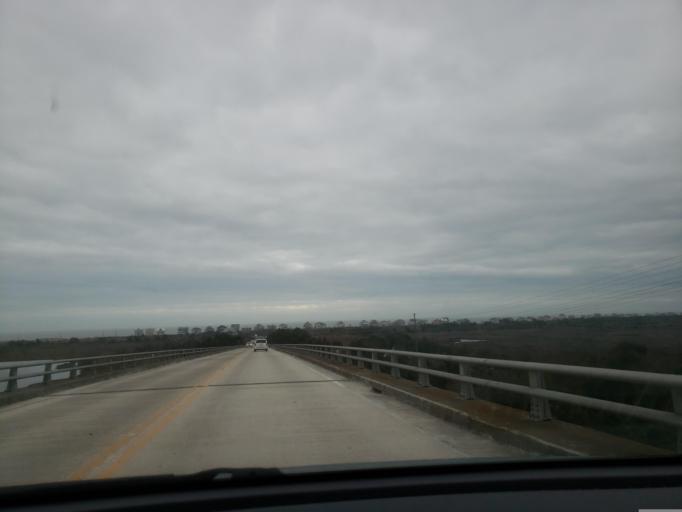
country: US
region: North Carolina
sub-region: Onslow County
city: Sneads Ferry
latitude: 34.4989
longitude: -77.4289
